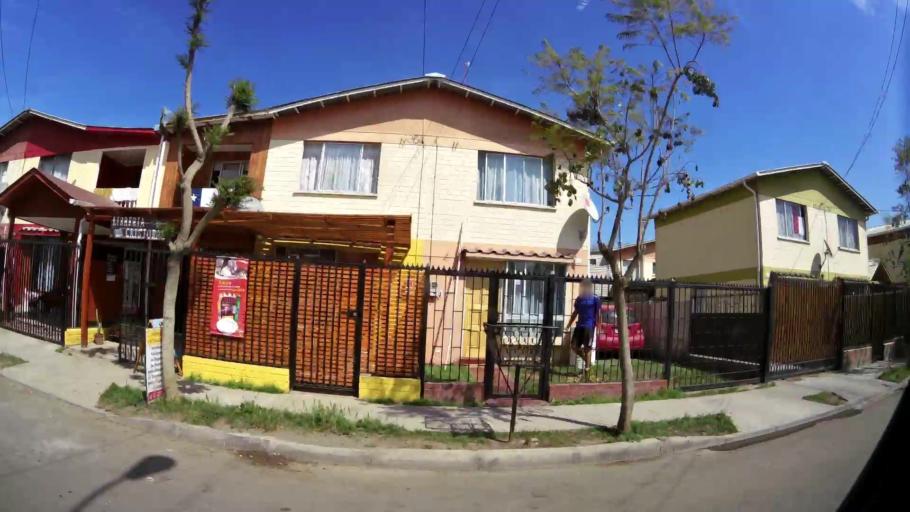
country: CL
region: Santiago Metropolitan
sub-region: Provincia de Talagante
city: Talagante
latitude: -33.6644
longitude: -70.9171
